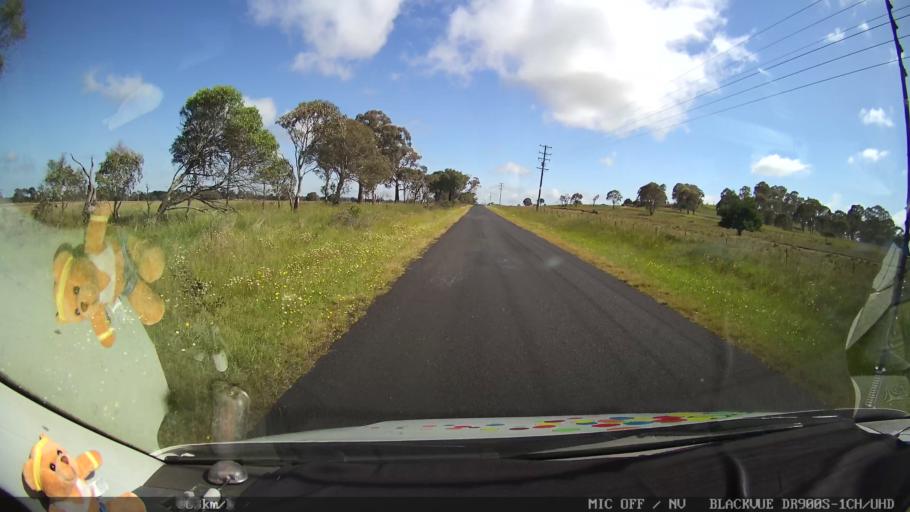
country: AU
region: New South Wales
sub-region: Guyra
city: Guyra
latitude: -30.1986
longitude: 151.6755
